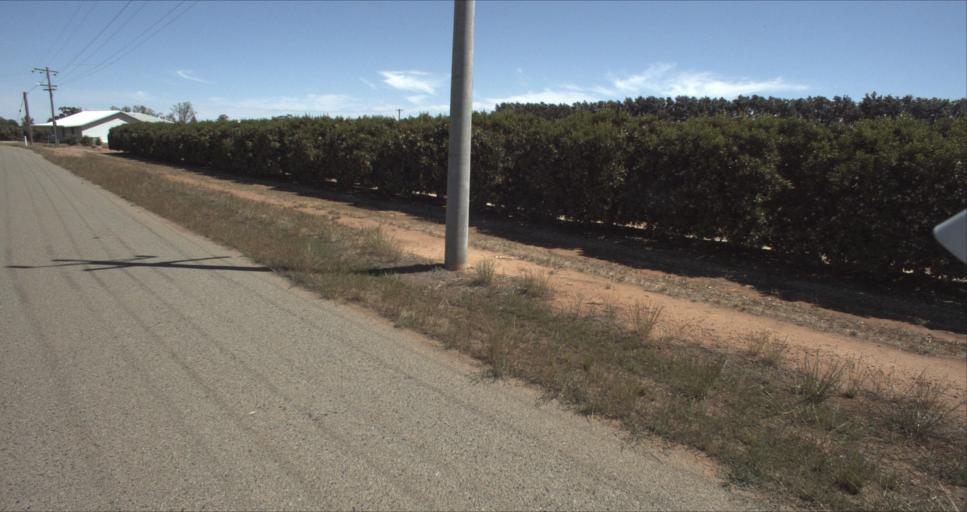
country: AU
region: New South Wales
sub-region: Leeton
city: Leeton
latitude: -34.5375
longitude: 146.3521
